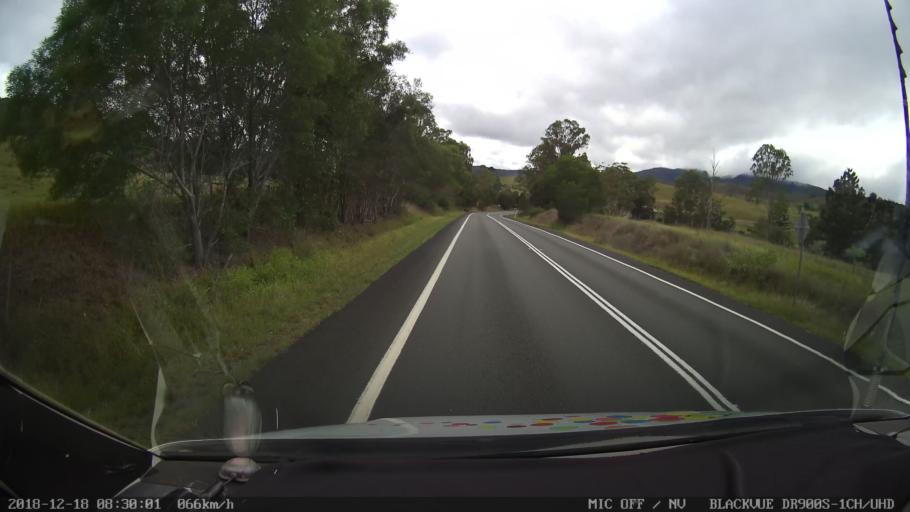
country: AU
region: New South Wales
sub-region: Kyogle
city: Kyogle
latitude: -28.3235
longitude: 152.7646
